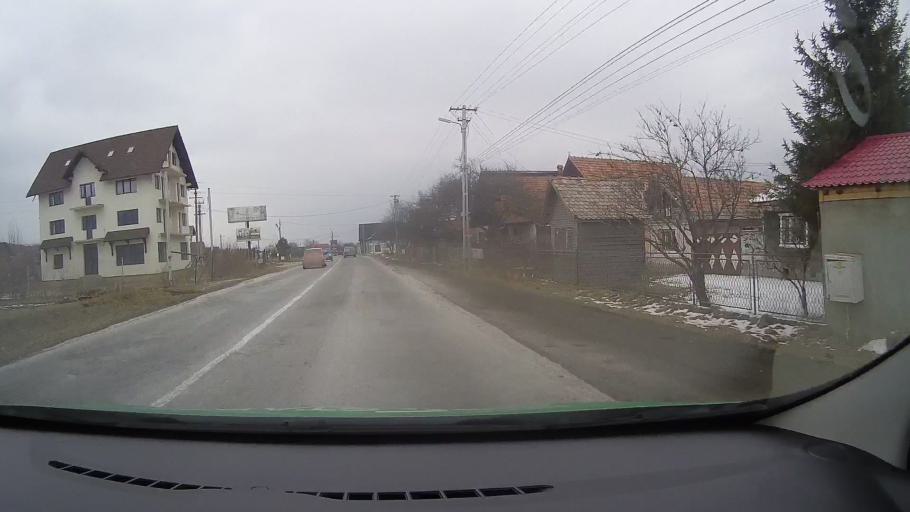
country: RO
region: Brasov
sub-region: Comuna Zarnesti
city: Tohanu Nou
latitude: 45.5337
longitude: 25.3751
